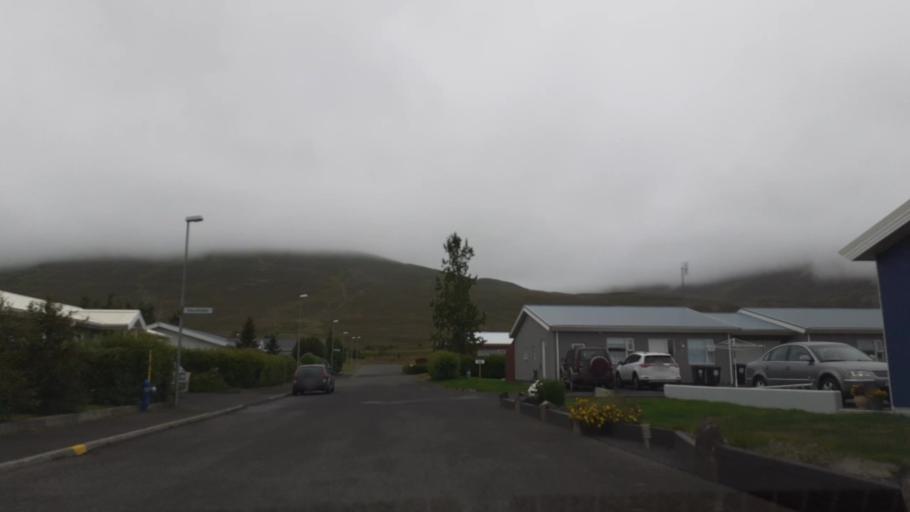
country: IS
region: Northeast
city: Dalvik
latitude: 65.9690
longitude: -18.5407
